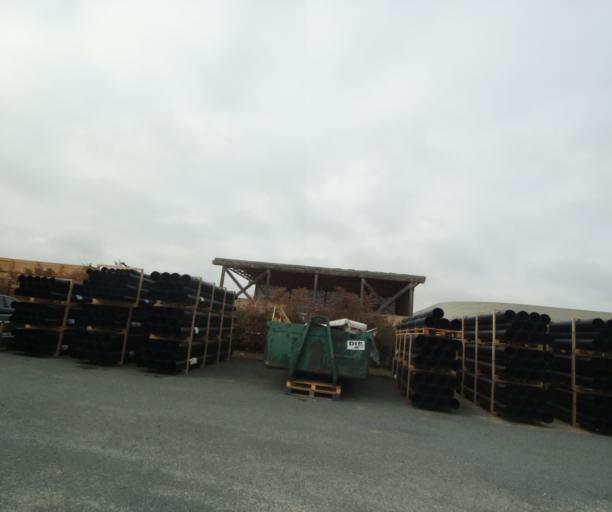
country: FR
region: Poitou-Charentes
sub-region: Departement de la Charente-Maritime
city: Saintes
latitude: 45.7437
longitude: -0.6659
